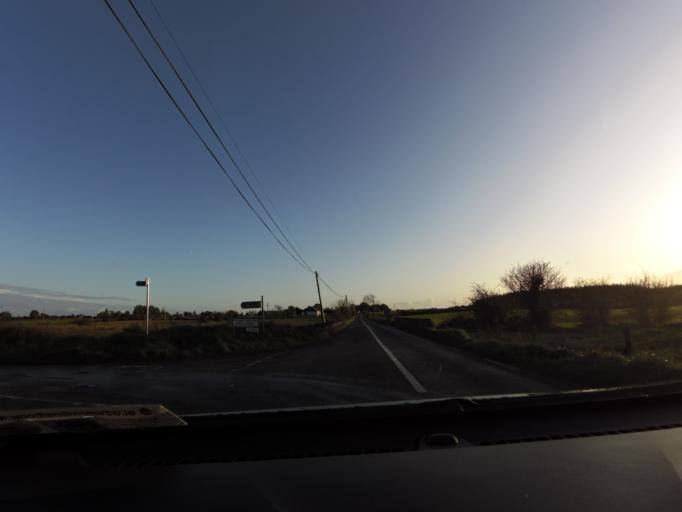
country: IE
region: Connaught
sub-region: Roscommon
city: Castlerea
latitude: 53.7144
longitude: -8.5632
